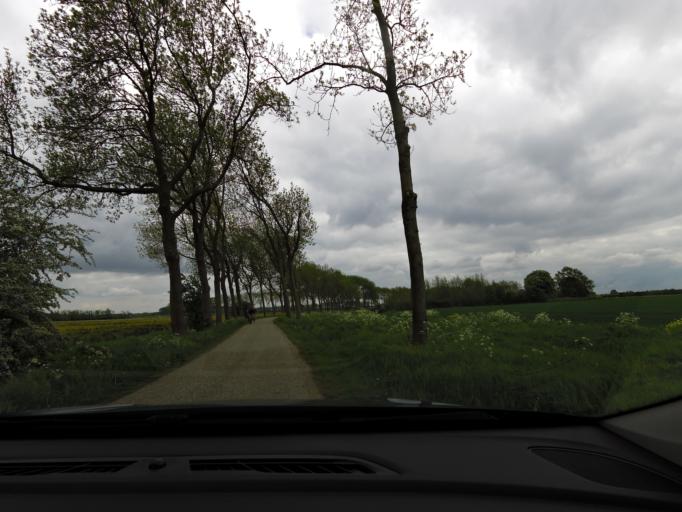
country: NL
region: Utrecht
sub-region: Gemeente Wijk bij Duurstede
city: Wijk bij Duurstede
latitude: 51.9111
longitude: 5.3470
